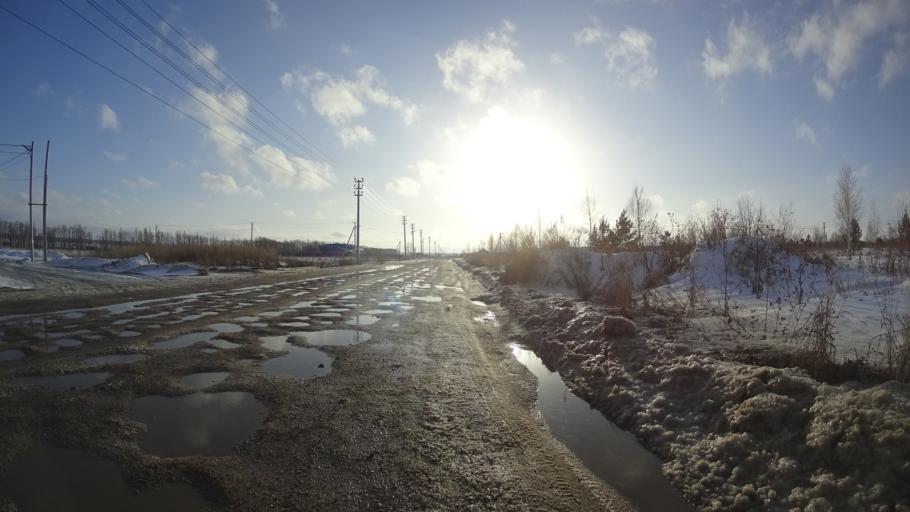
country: RU
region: Chelyabinsk
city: Sargazy
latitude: 55.1086
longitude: 61.2723
